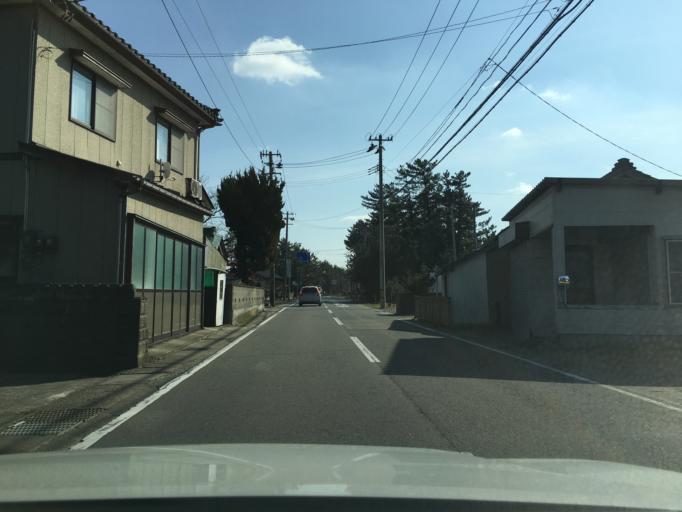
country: JP
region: Yamagata
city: Tsuruoka
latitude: 38.8210
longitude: 139.7786
